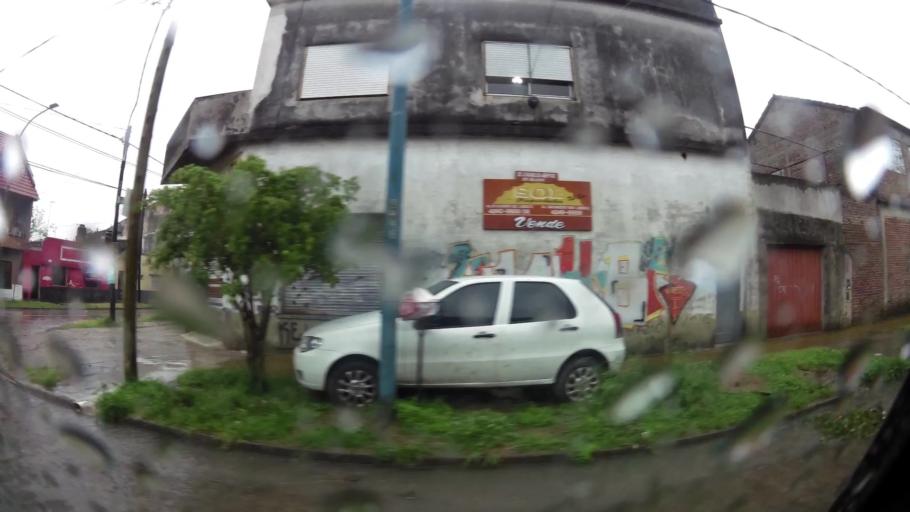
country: AR
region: Buenos Aires
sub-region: Partido de Lanus
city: Lanus
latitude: -34.7120
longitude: -58.4053
